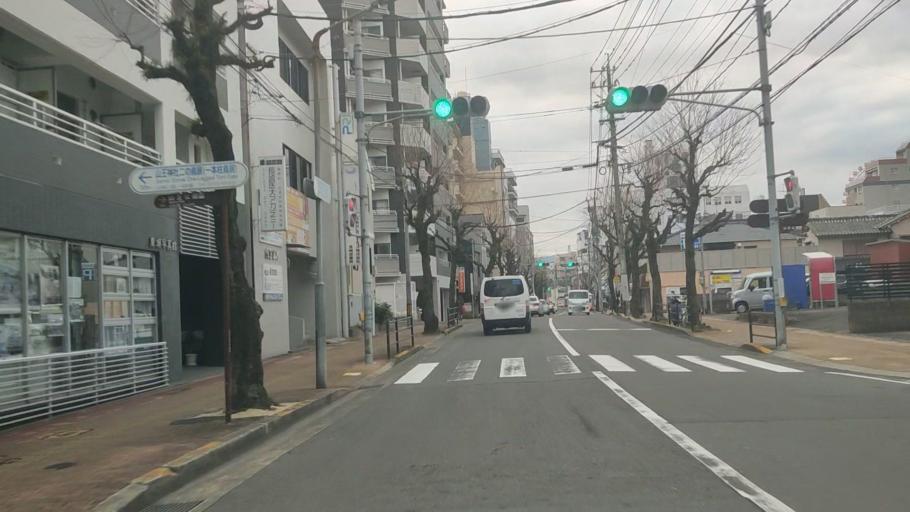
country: JP
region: Nagasaki
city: Nagasaki-shi
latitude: 32.7675
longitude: 129.8668
